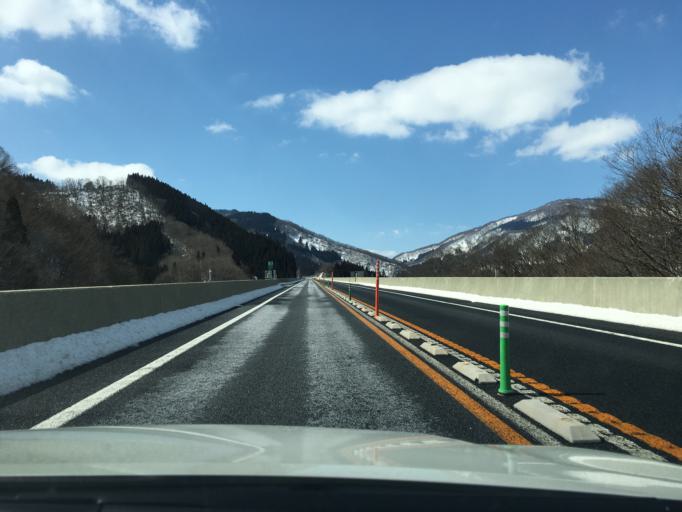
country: JP
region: Yamagata
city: Sagae
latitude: 38.4417
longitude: 140.0658
